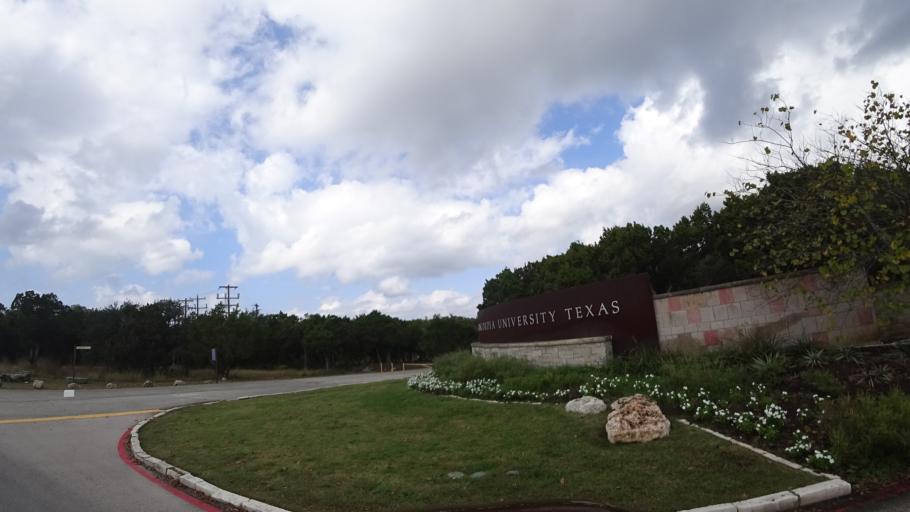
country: US
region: Texas
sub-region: Williamson County
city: Anderson Mill
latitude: 30.4202
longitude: -97.8396
